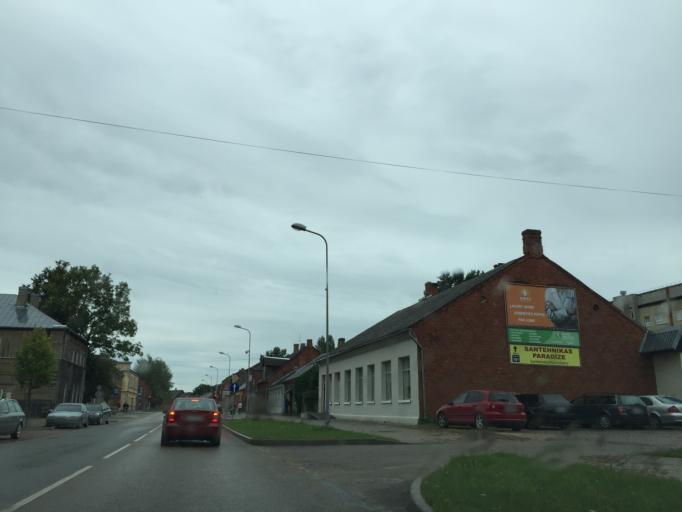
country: LV
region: Jekabpils Rajons
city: Jekabpils
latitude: 56.5051
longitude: 25.8650
